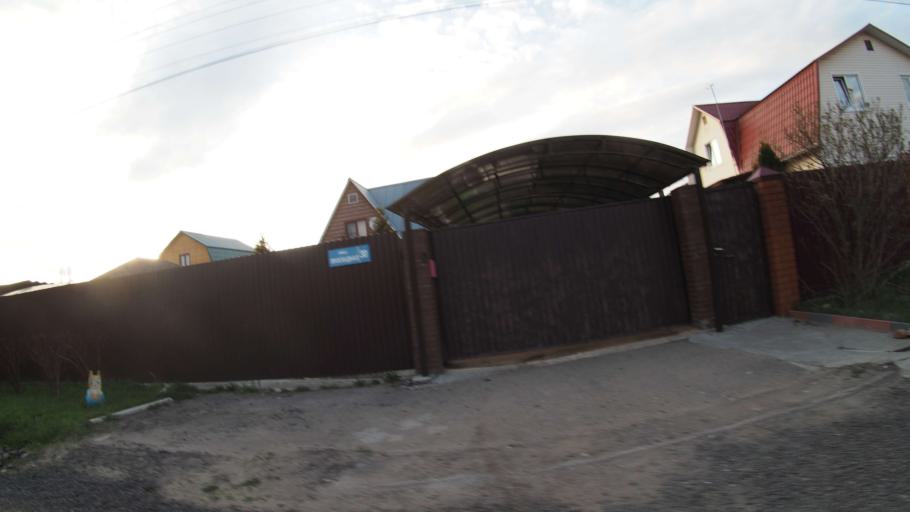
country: RU
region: Moskovskaya
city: Ramenskoye
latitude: 55.5677
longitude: 38.2792
